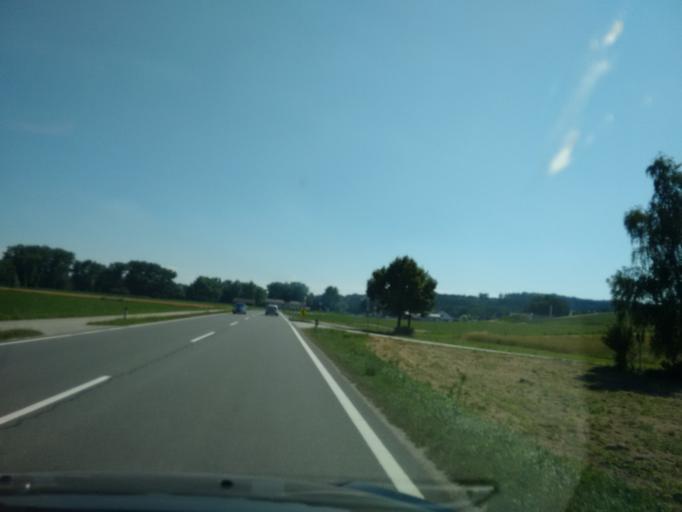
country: AT
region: Upper Austria
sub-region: Wels-Land
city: Buchkirchen
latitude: 48.2571
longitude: 13.9741
